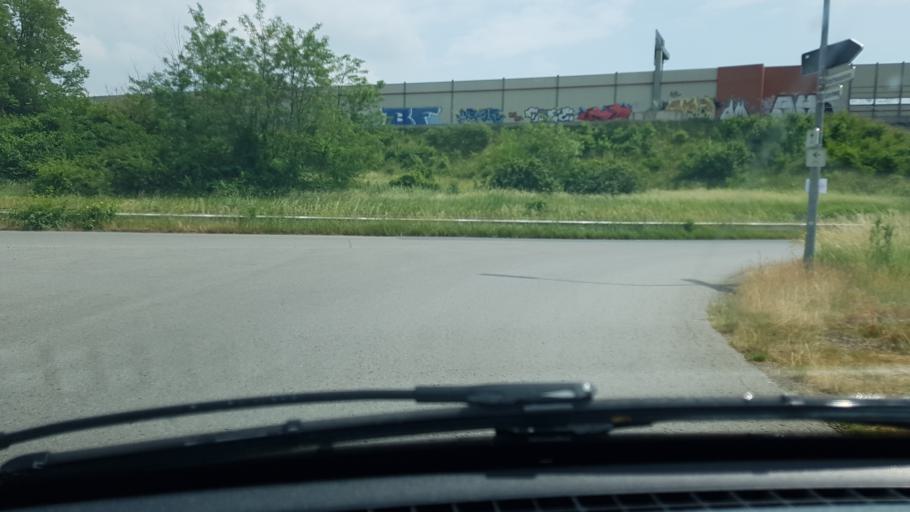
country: DE
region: Lower Saxony
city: Leiferde
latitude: 52.2341
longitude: 10.5113
